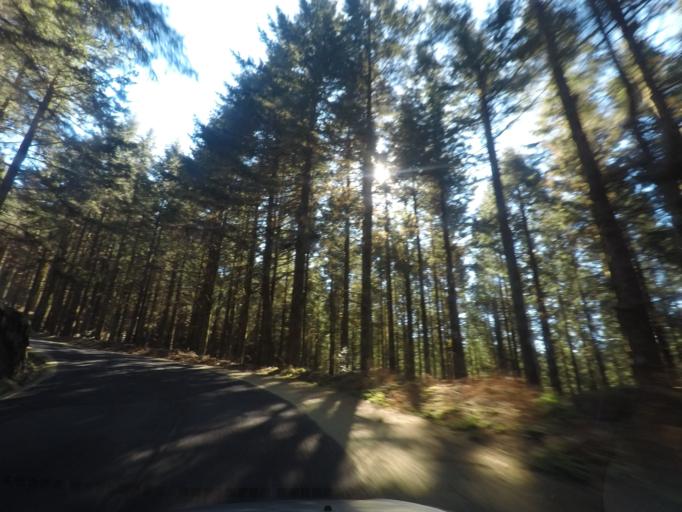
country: PT
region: Madeira
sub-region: Funchal
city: Nossa Senhora do Monte
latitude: 32.7187
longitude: -16.8845
